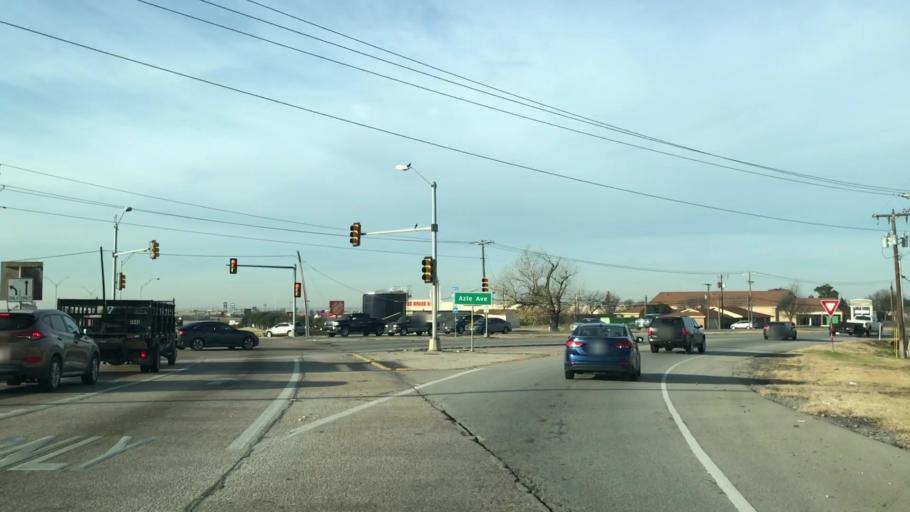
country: US
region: Texas
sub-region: Tarrant County
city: Sansom Park
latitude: 32.8143
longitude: -97.4137
